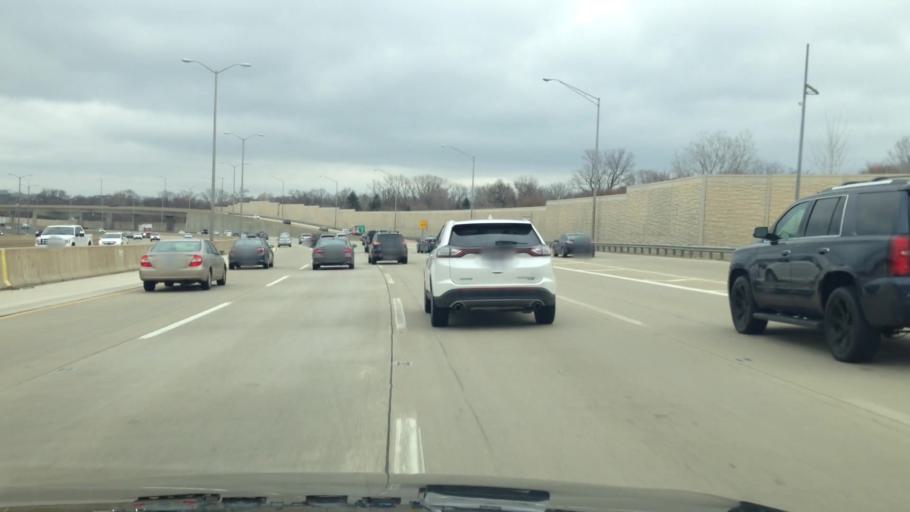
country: US
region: Illinois
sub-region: DuPage County
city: Downers Grove
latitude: 41.8108
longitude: -88.0317
